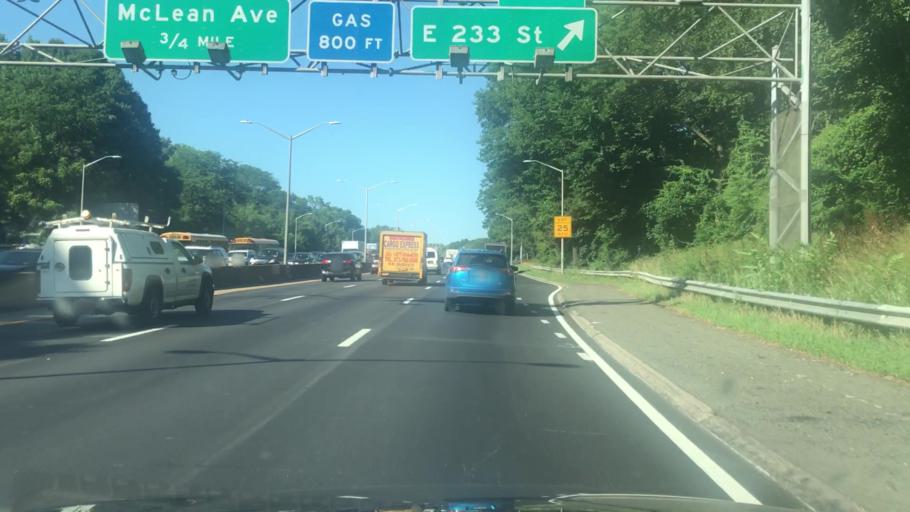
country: US
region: New York
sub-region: Westchester County
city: Yonkers
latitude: 40.8924
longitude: -73.8843
